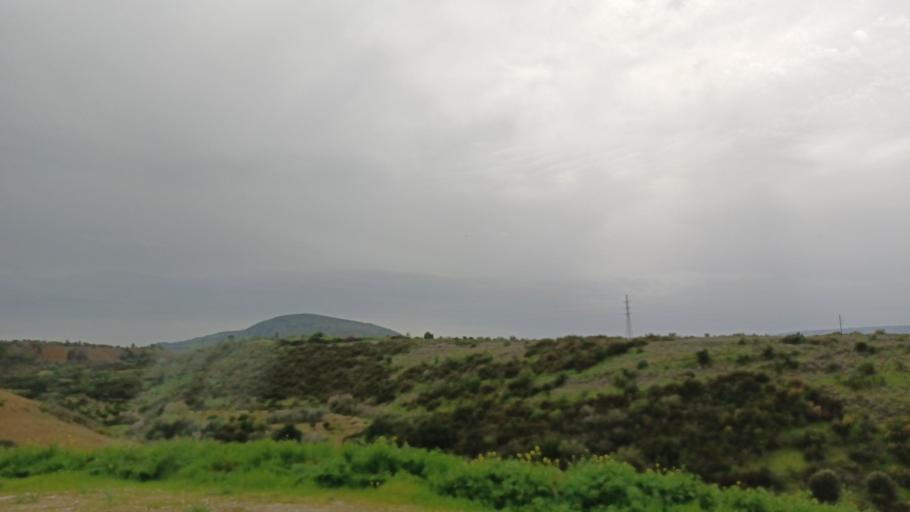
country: CY
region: Pafos
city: Polis
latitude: 35.0494
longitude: 32.4752
